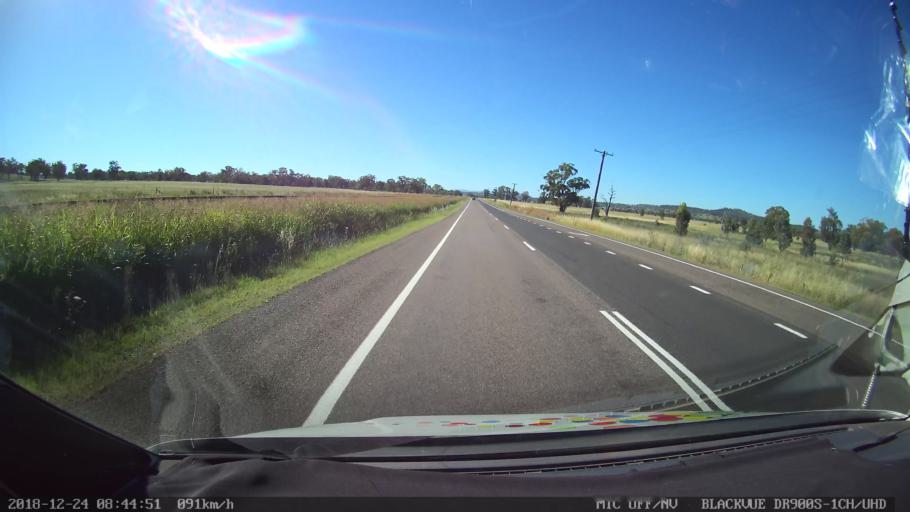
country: AU
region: New South Wales
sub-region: Liverpool Plains
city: Quirindi
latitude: -31.4072
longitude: 150.6499
